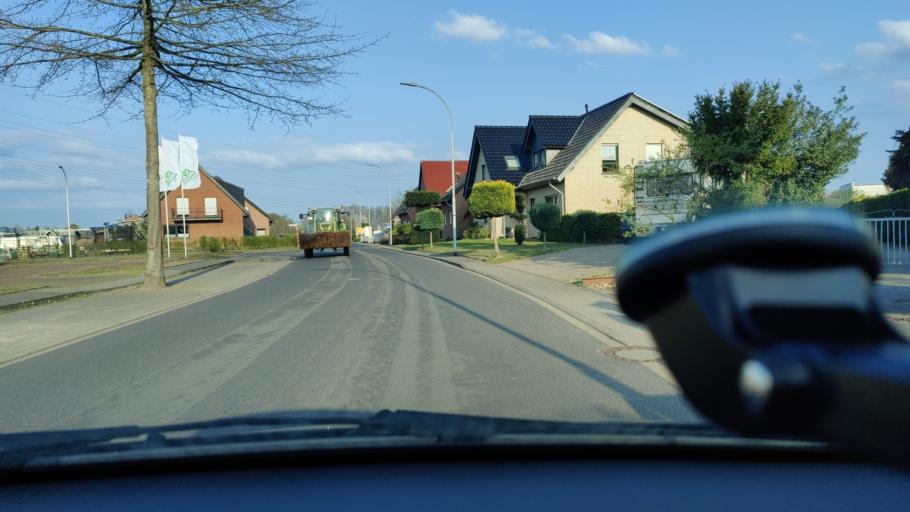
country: DE
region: North Rhine-Westphalia
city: Straelen
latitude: 51.4342
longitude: 6.2709
